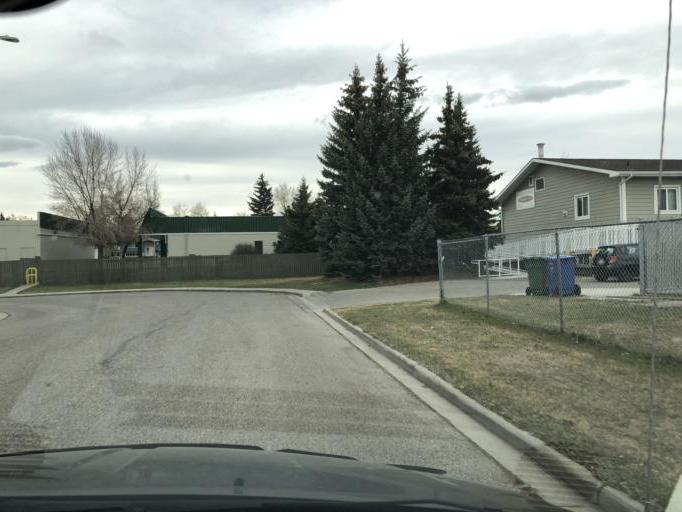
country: CA
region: Alberta
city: Calgary
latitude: 50.9414
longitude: -114.0322
